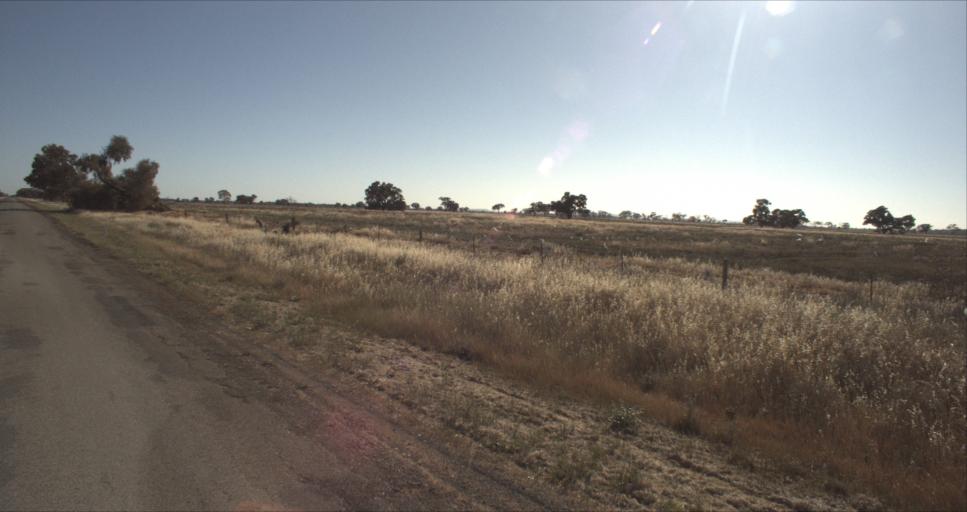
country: AU
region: New South Wales
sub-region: Leeton
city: Leeton
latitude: -34.6006
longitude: 146.2578
